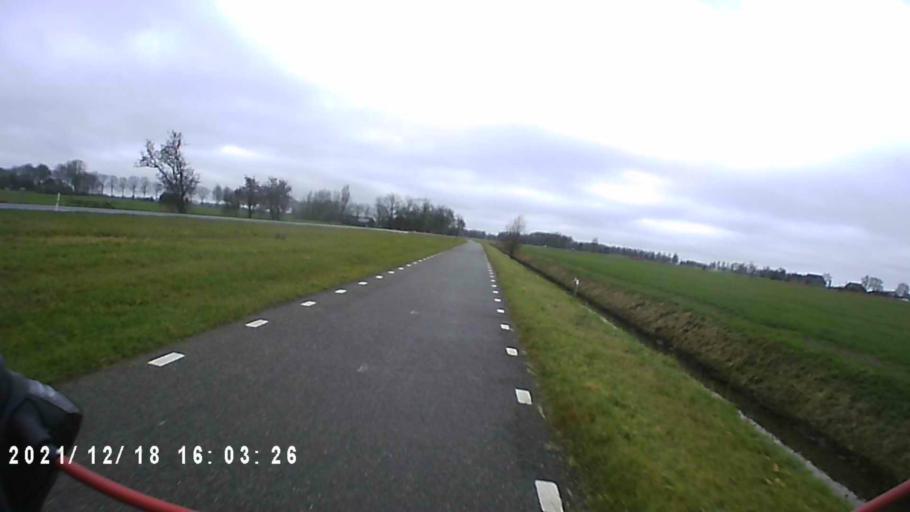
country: NL
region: Friesland
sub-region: Gemeente Dongeradeel
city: Anjum
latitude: 53.3496
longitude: 6.0809
